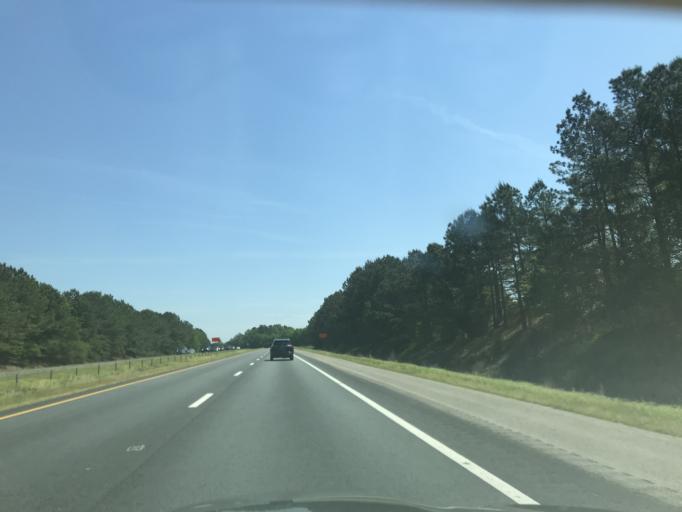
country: US
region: North Carolina
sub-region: Johnston County
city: Benson
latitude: 35.3754
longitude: -78.5038
